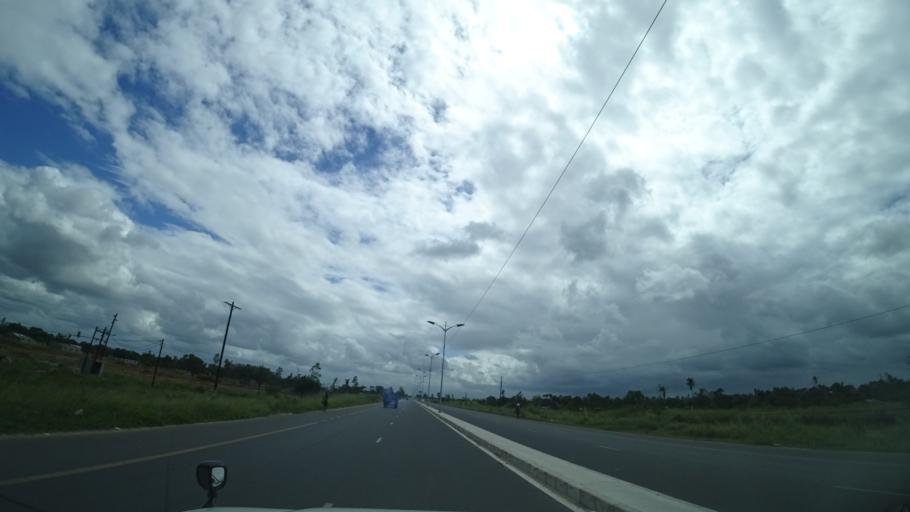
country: MZ
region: Sofala
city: Dondo
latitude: -19.6015
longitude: 34.7412
